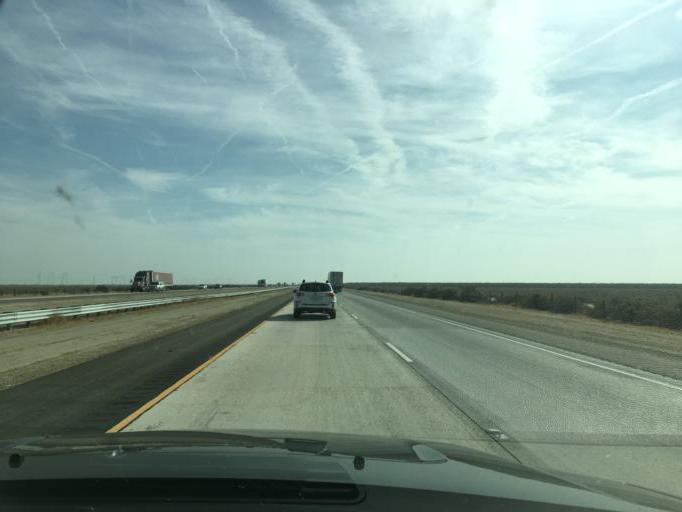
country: US
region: California
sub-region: Kern County
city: Lost Hills
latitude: 35.5471
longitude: -119.5863
